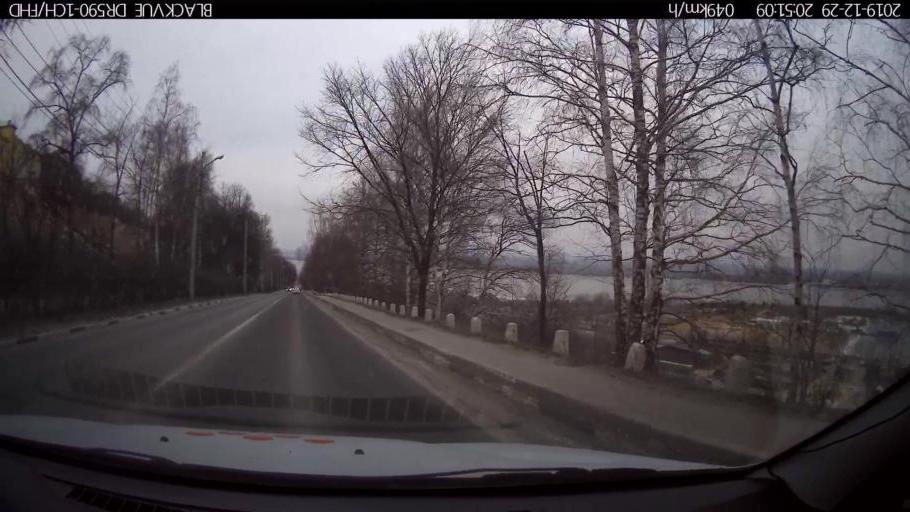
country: RU
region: Nizjnij Novgorod
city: Nizhniy Novgorod
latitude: 56.3256
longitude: 44.0343
